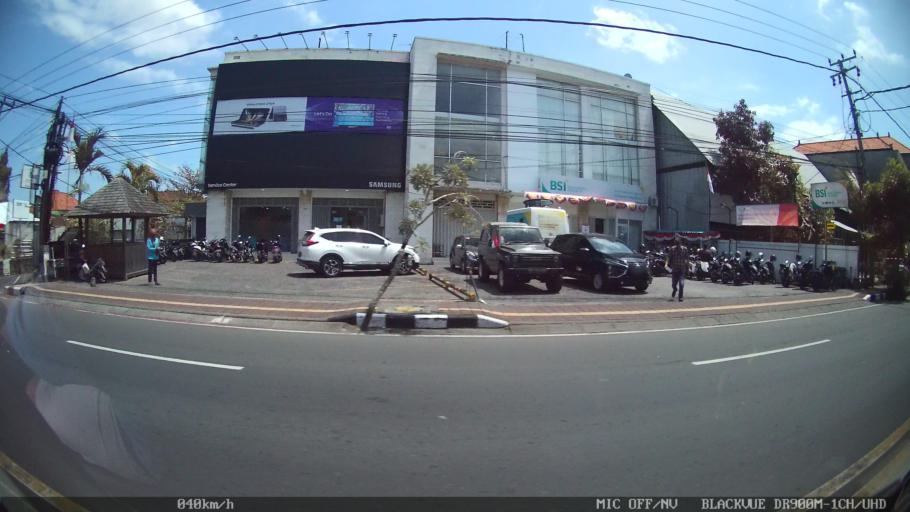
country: ID
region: Bali
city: Denpasar
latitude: -8.6581
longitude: 115.1915
